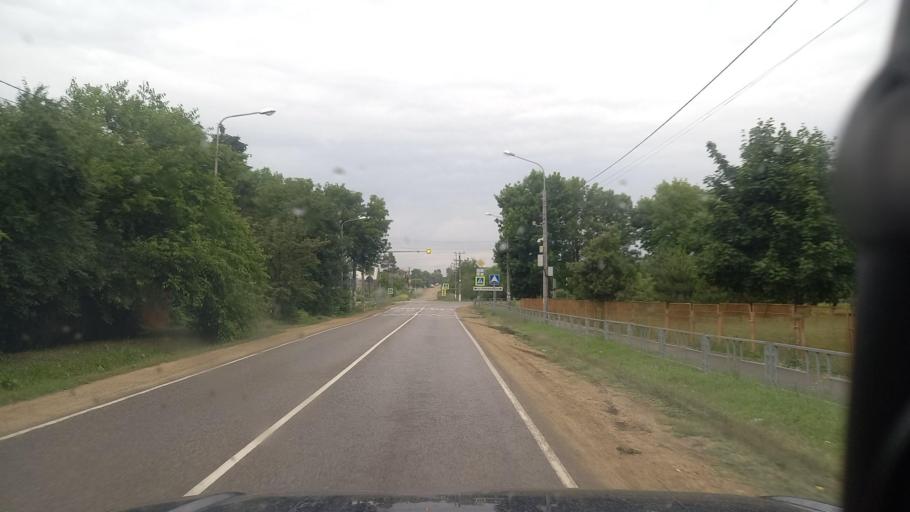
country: RU
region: Krasnodarskiy
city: Ryazanskaya
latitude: 44.9546
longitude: 39.5903
